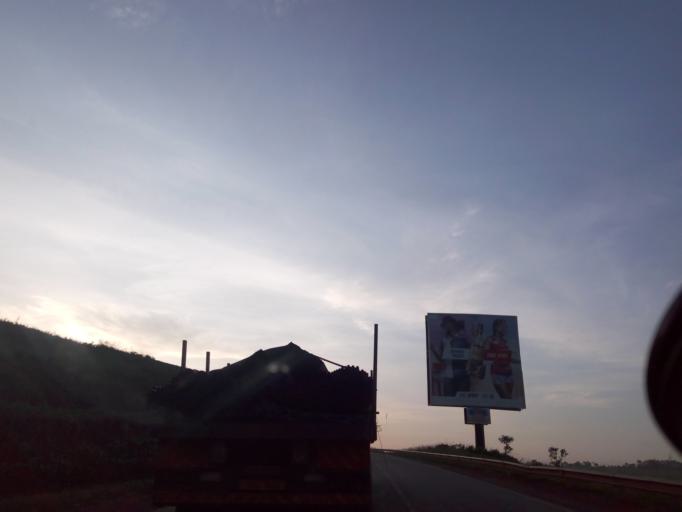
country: UG
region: Central Region
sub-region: Buikwe District
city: Njeru
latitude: 0.4075
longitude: 33.0791
